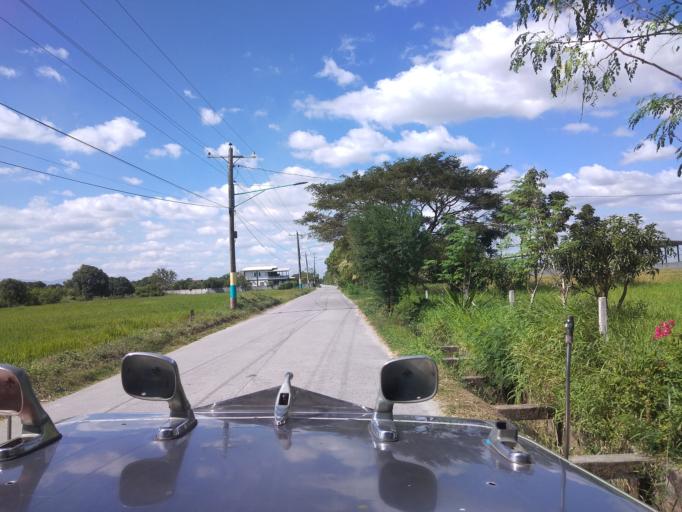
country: PH
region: Central Luzon
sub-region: Province of Pampanga
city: Bacolor
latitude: 15.0211
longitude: 120.6390
